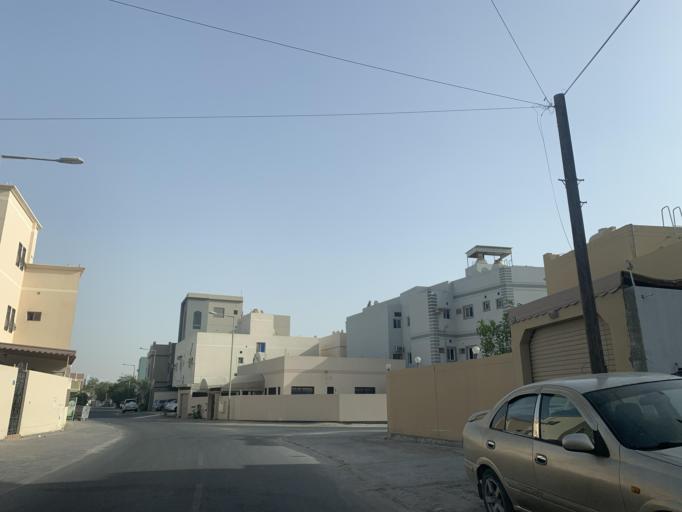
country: BH
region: Northern
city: Madinat `Isa
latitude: 26.1606
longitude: 50.5121
